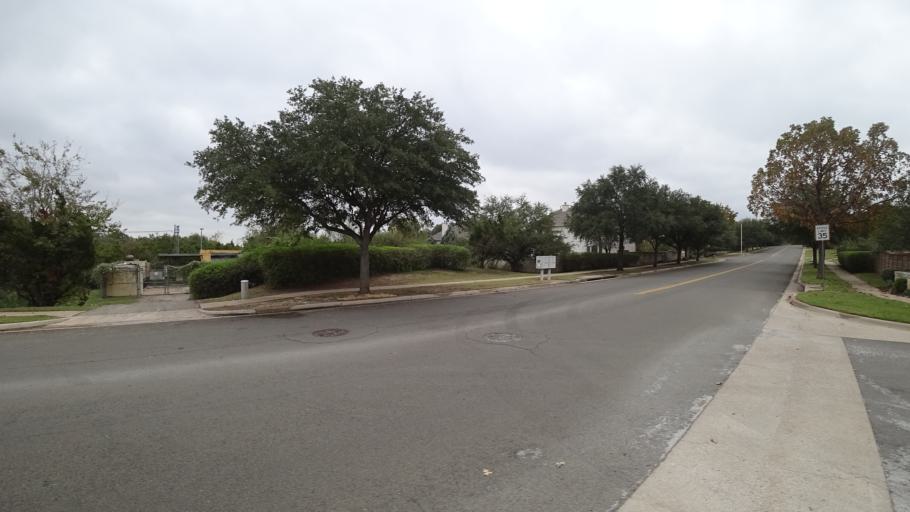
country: US
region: Texas
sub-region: Williamson County
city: Anderson Mill
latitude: 30.4328
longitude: -97.8311
